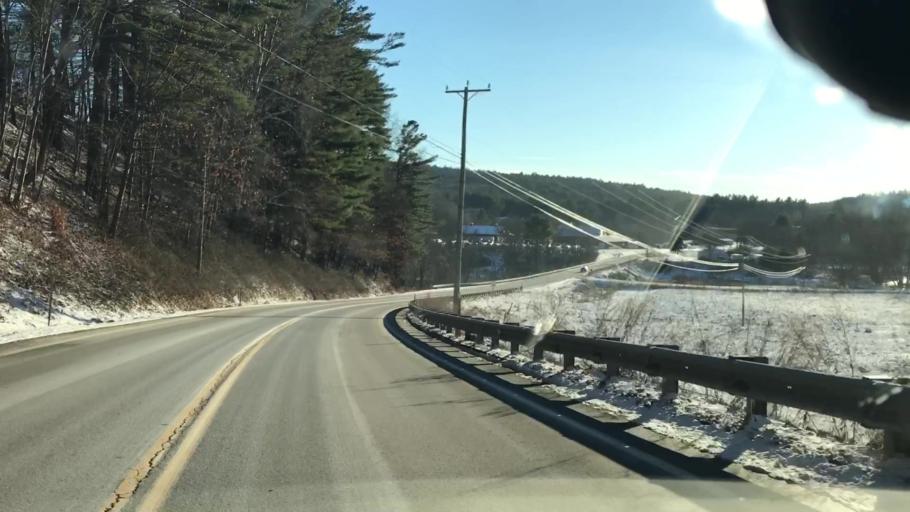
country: US
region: New Hampshire
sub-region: Grafton County
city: North Haverhill
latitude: 44.0817
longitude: -72.0260
